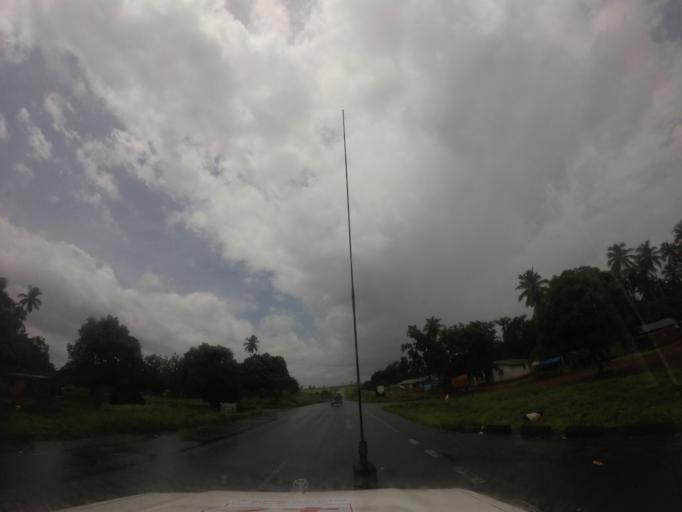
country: SL
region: Southern Province
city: Rotifunk
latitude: 8.4859
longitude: -12.7679
